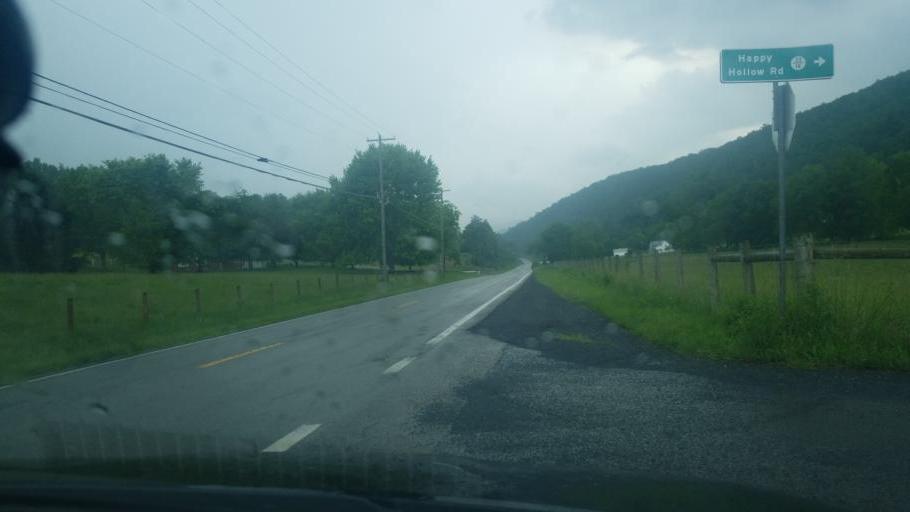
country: US
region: West Virginia
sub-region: Pendleton County
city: Franklin
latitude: 38.6703
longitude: -79.3058
